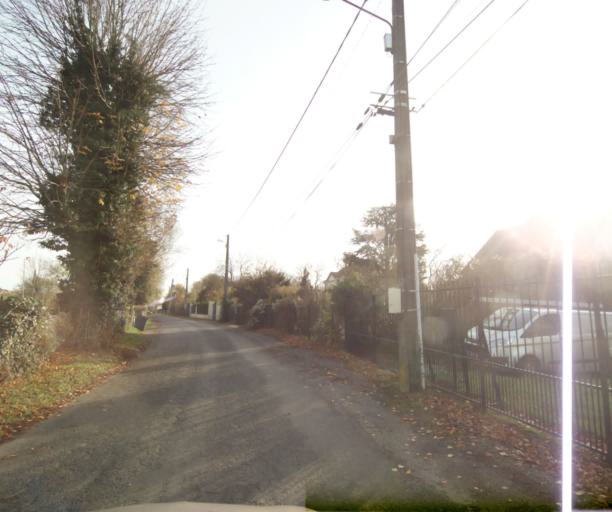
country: FR
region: Ile-de-France
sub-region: Departement des Yvelines
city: Maisons-Laffitte
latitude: 48.9813
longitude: 2.1380
